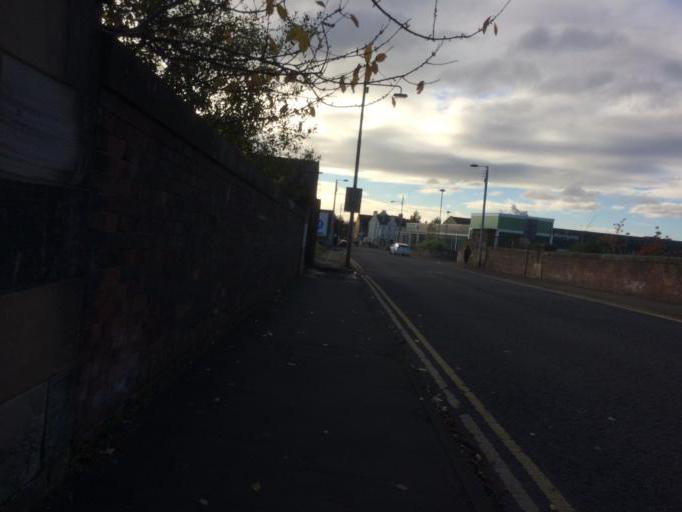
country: GB
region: Scotland
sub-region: Glasgow City
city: Glasgow
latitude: 55.8575
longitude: -4.2323
